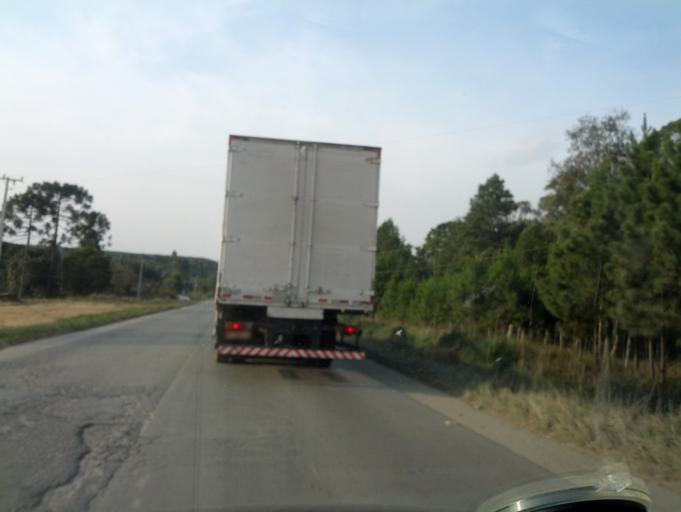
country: BR
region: Santa Catarina
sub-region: Otacilio Costa
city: Otacilio Costa
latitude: -27.5212
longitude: -50.1350
